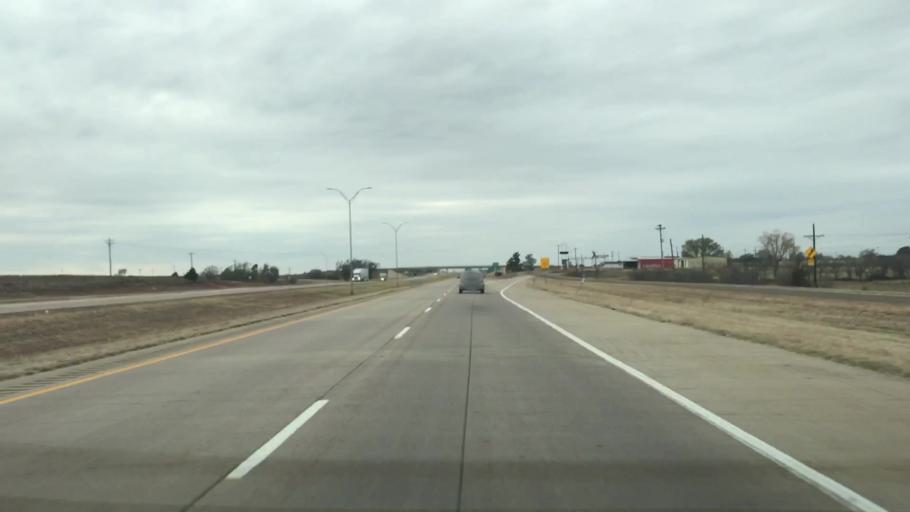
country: US
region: Texas
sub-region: Wheeler County
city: Shamrock
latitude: 35.2270
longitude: -100.1580
